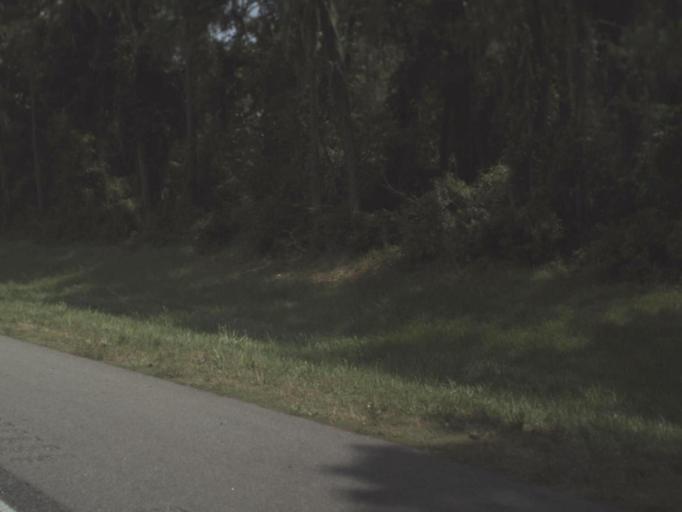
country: US
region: Florida
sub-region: Suwannee County
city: Wellborn
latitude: 30.3600
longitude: -82.8463
